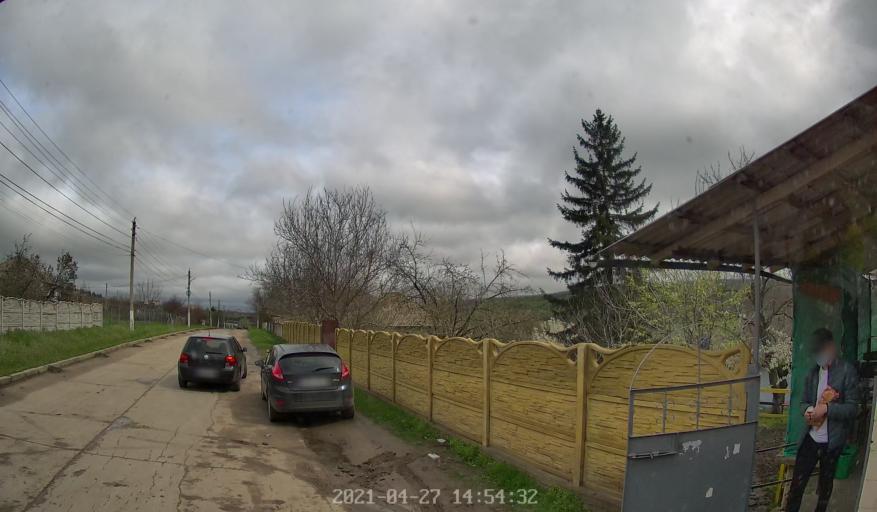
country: MD
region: Chisinau
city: Vadul lui Voda
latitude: 47.0472
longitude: 29.0596
